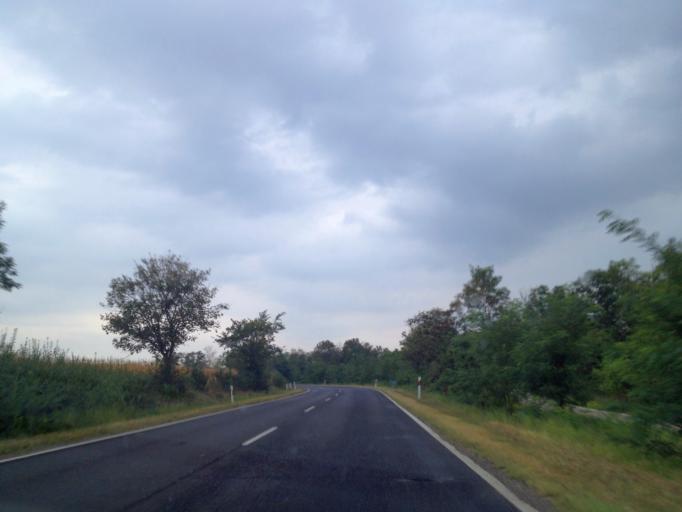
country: AT
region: Burgenland
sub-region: Politischer Bezirk Neusiedl am See
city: Nickelsdorf
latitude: 47.9256
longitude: 17.1261
